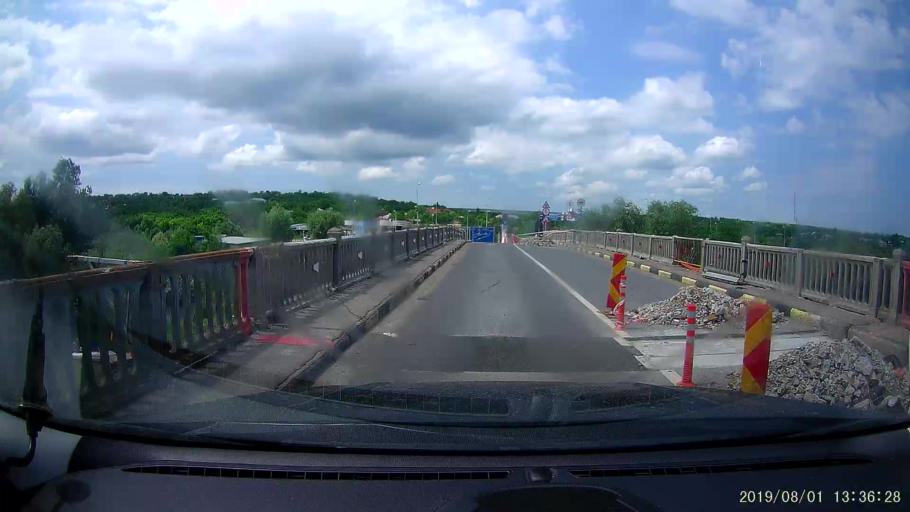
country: RO
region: Galati
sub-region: Comuna Oancea
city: Oancea
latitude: 45.9174
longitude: 28.1204
